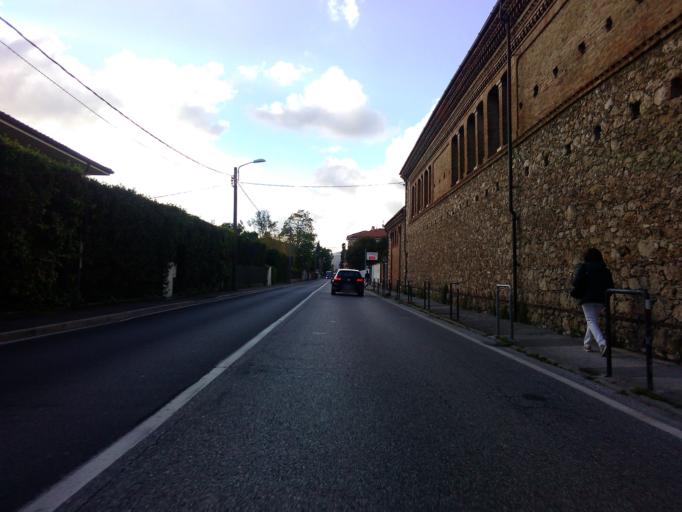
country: IT
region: Tuscany
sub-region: Provincia di Lucca
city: Pietrasanta
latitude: 43.9615
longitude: 10.2264
